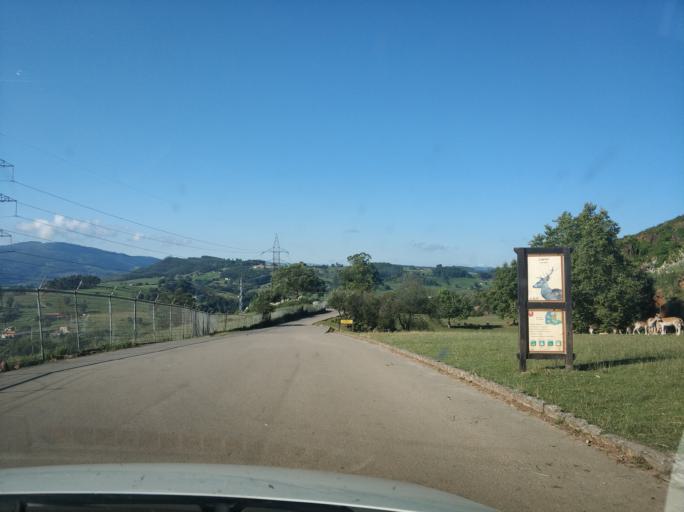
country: ES
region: Cantabria
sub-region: Provincia de Cantabria
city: Penagos
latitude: 43.3463
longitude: -3.8476
